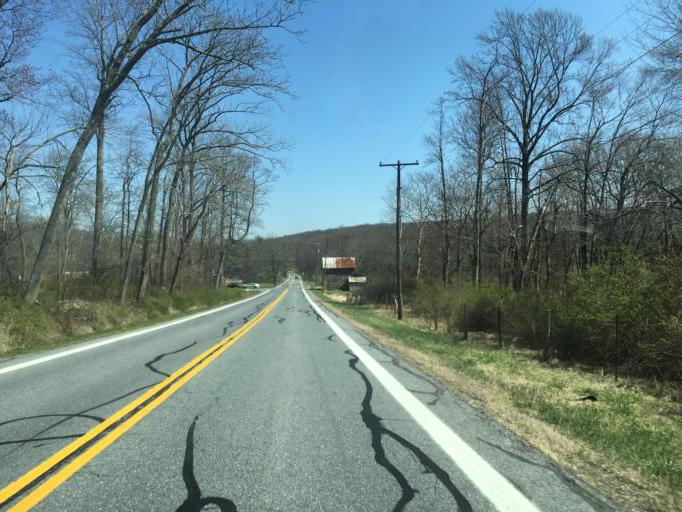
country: US
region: Maryland
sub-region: Washington County
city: Smithsburg
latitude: 39.6365
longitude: -77.4987
